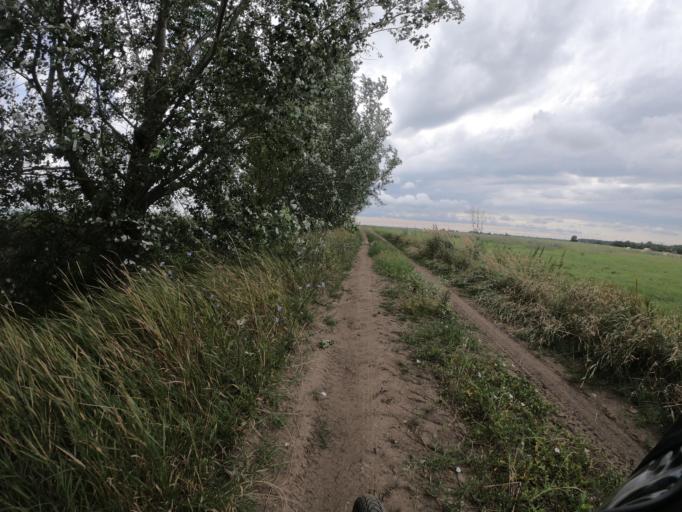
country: HU
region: Jasz-Nagykun-Szolnok
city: Tiszafured
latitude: 47.7131
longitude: 20.7819
